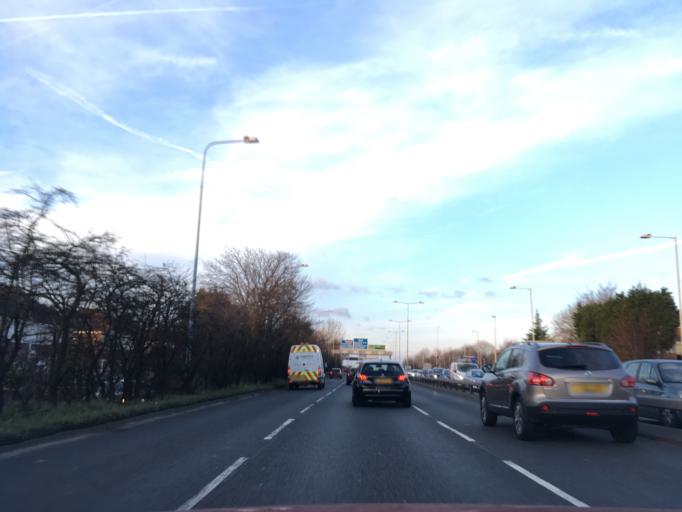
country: GB
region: England
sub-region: Manchester
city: Didsbury
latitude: 53.3935
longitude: -2.2266
